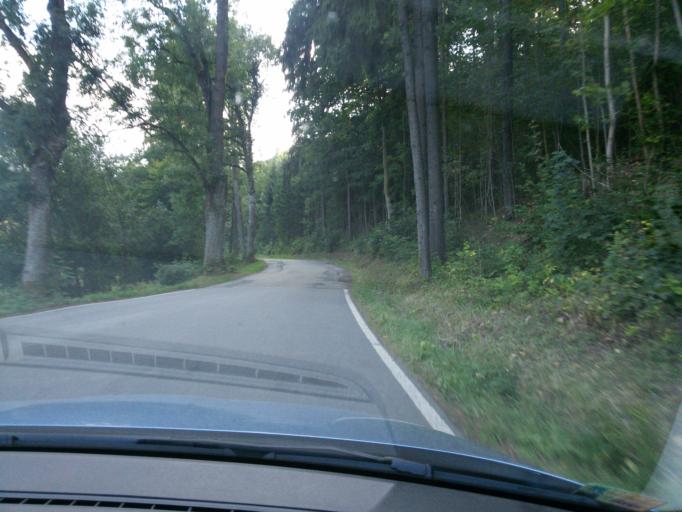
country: CZ
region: South Moravian
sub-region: Okres Brno-Venkov
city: Lomnice
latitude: 49.4549
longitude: 16.4357
